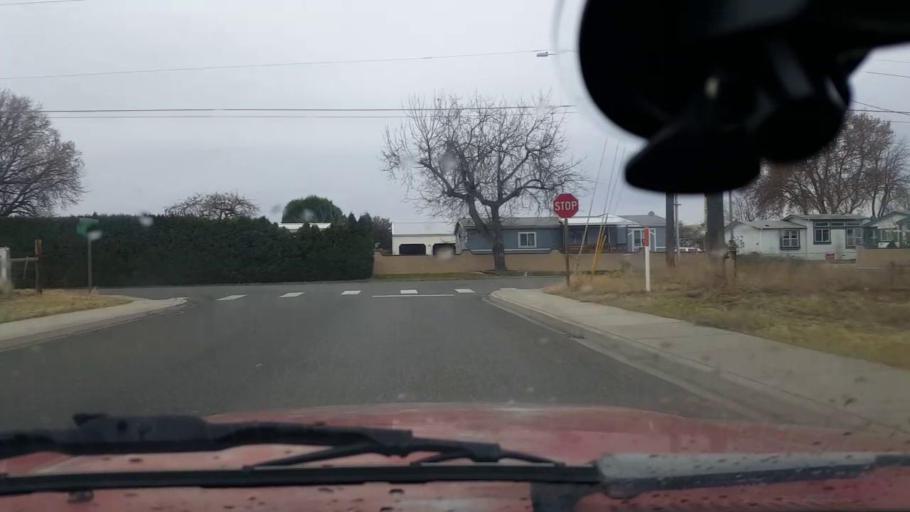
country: US
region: Washington
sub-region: Asotin County
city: Clarkston Heights-Vineland
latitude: 46.3857
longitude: -117.0827
